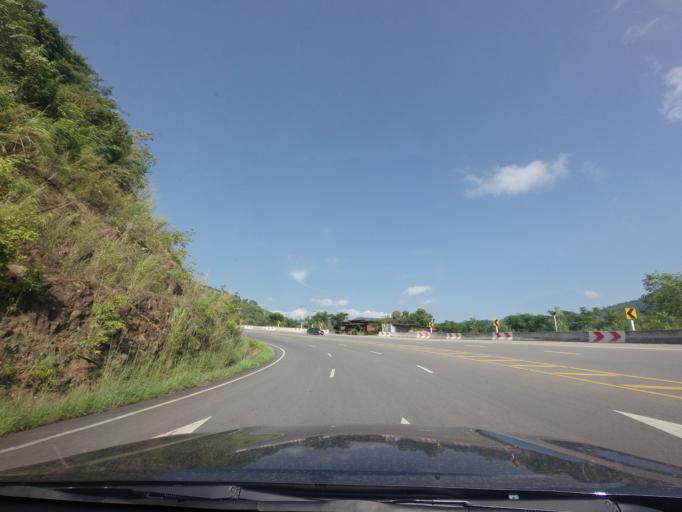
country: TH
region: Phetchabun
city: Lom Sak
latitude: 16.7728
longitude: 101.1252
